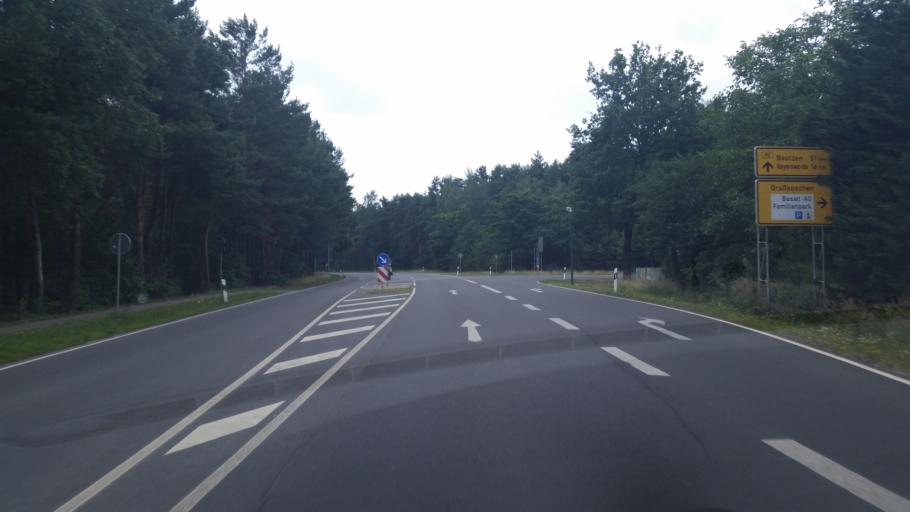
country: DE
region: Brandenburg
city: Senftenberg
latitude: 51.4882
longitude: 14.0679
